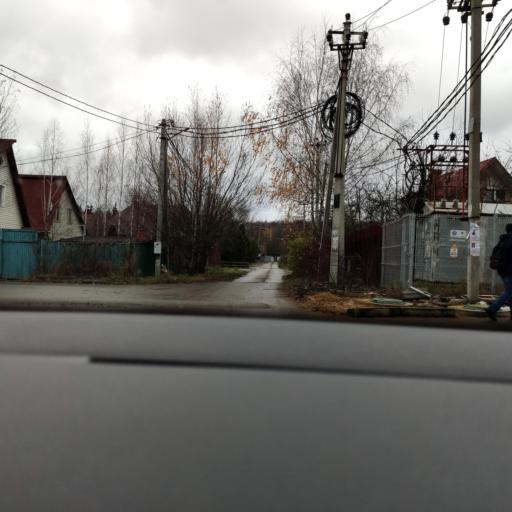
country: RU
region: Moscow
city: Gol'yanovo
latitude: 55.8336
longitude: 37.8346
